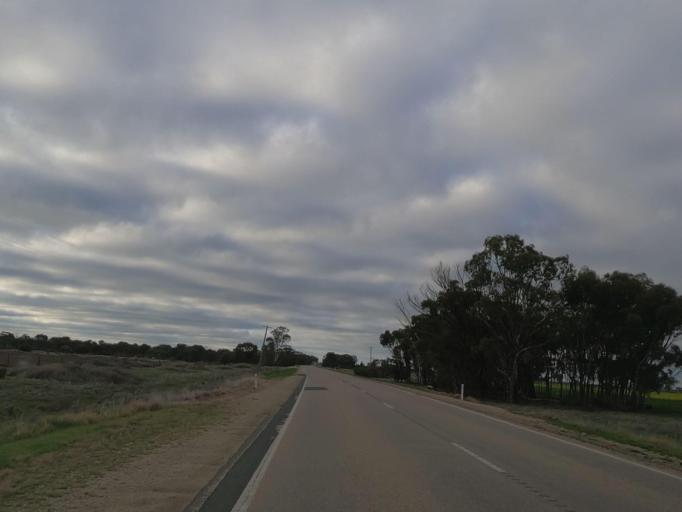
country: AU
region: Victoria
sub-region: Swan Hill
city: Swan Hill
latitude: -35.8240
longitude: 143.9482
